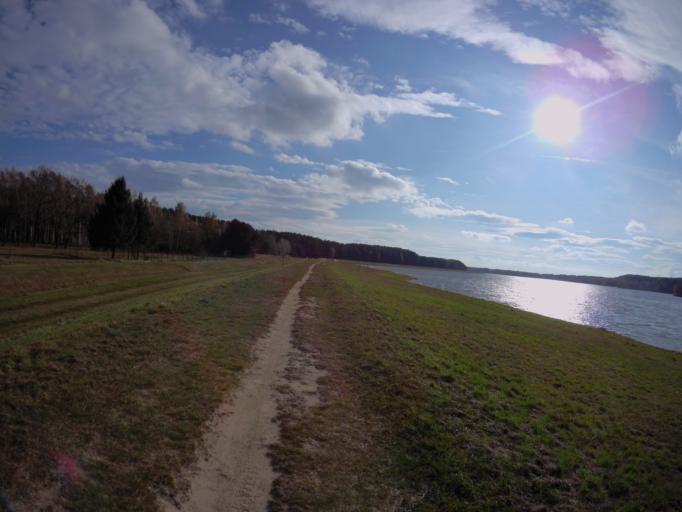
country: PL
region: Subcarpathian Voivodeship
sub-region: Powiat kolbuszowski
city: Lipnica
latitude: 50.3378
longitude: 21.9418
